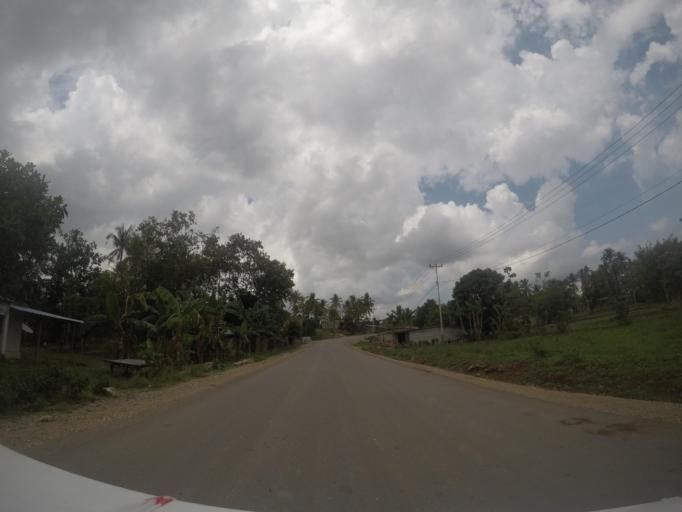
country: TL
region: Baucau
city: Baucau
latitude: -8.5399
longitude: 126.4163
